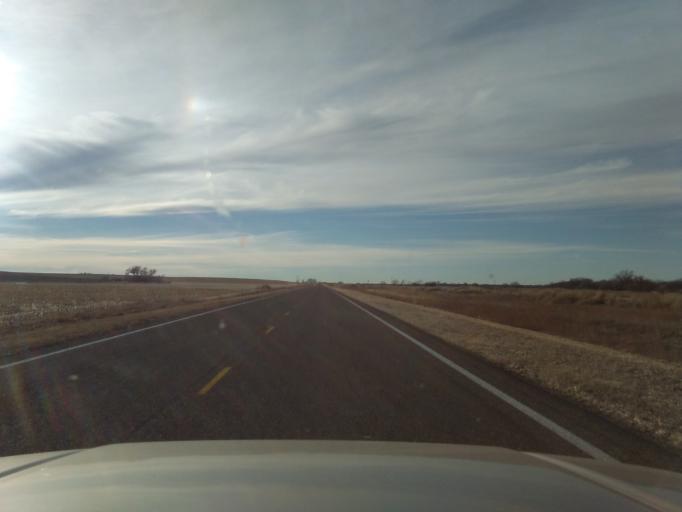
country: US
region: Kansas
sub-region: Norton County
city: Norton
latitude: 39.7545
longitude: -100.1266
